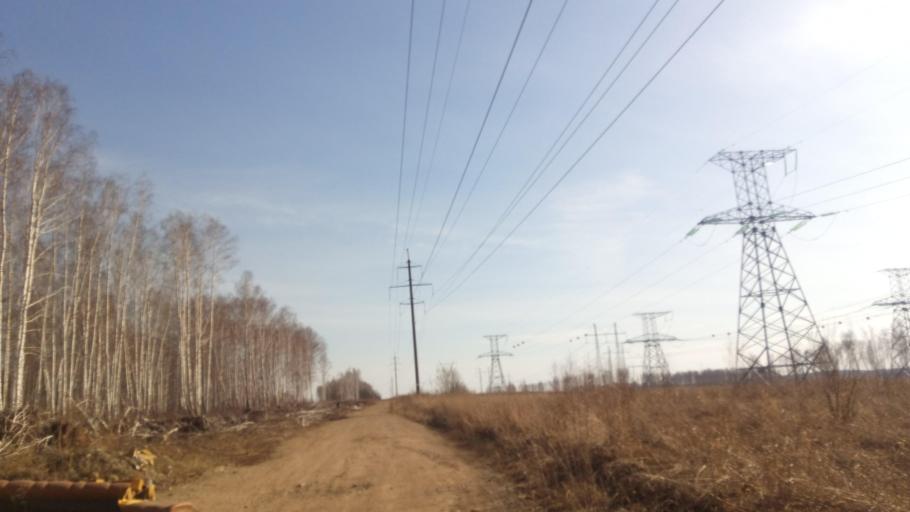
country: RU
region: Chelyabinsk
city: Sargazy
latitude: 55.1173
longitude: 61.2364
